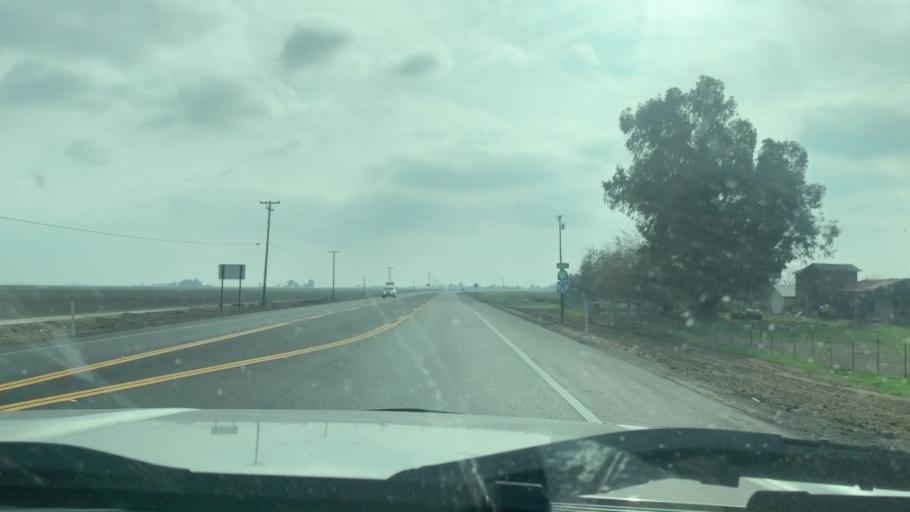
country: US
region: California
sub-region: Kings County
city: Stratford
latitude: 36.2113
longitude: -119.8162
